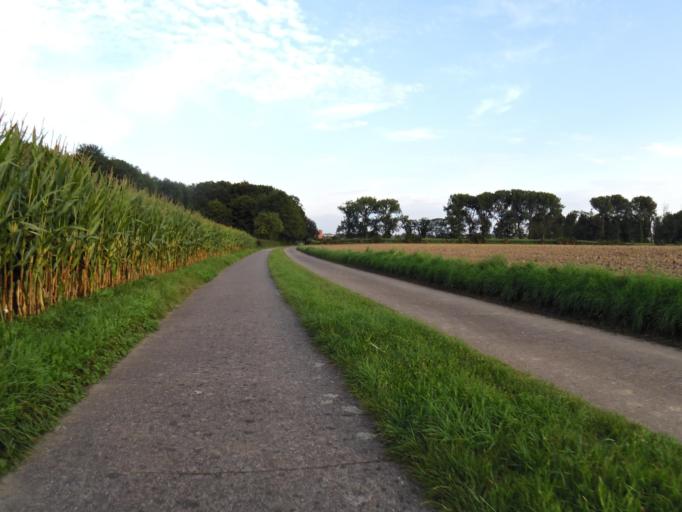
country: BE
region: Flanders
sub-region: Provincie Limburg
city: Tongeren
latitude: 50.7757
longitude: 5.5006
